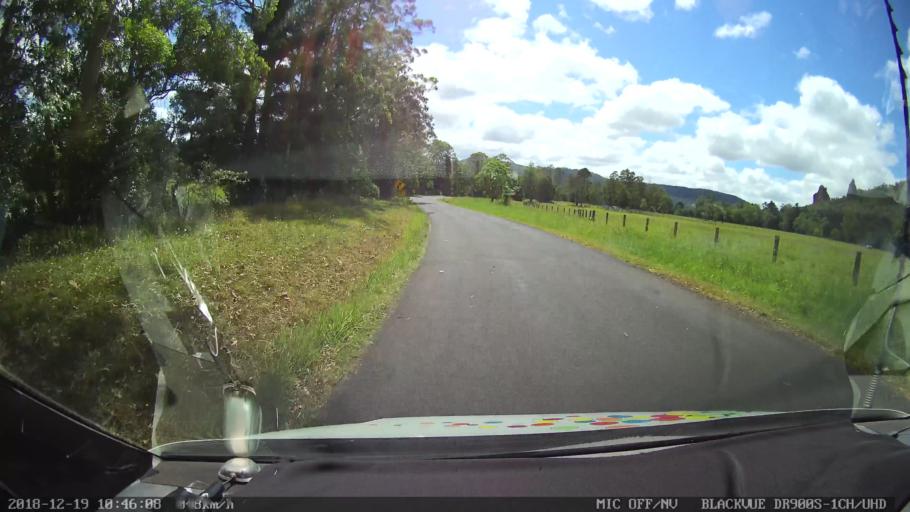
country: AU
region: New South Wales
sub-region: Lismore Municipality
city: Nimbin
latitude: -28.6000
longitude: 153.1951
